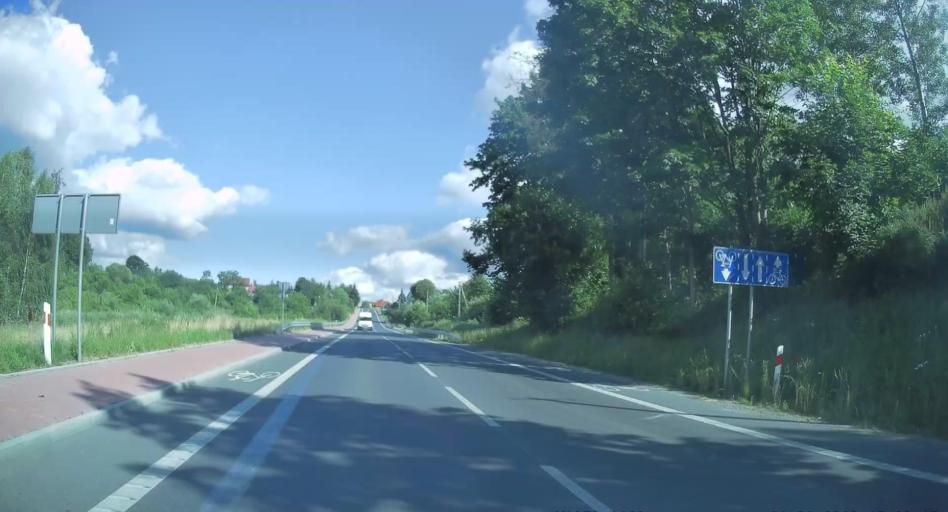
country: PL
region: Swietokrzyskie
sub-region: Powiat kielecki
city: Bodzentyn
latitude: 50.9386
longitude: 20.9510
